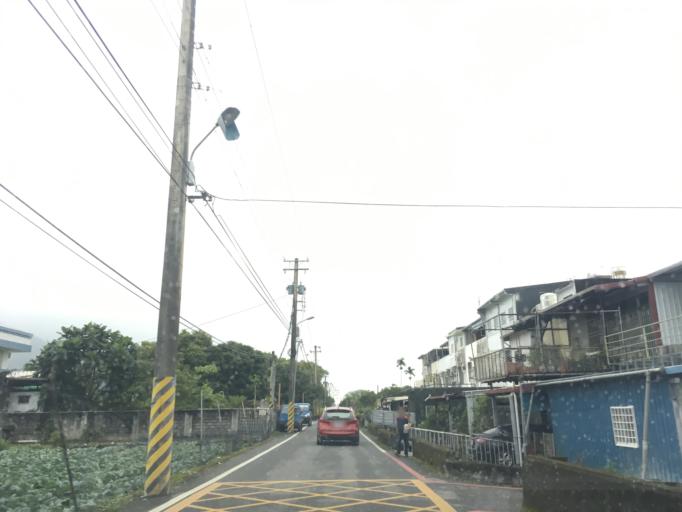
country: TW
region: Taiwan
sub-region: Hualien
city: Hualian
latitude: 23.9864
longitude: 121.5684
